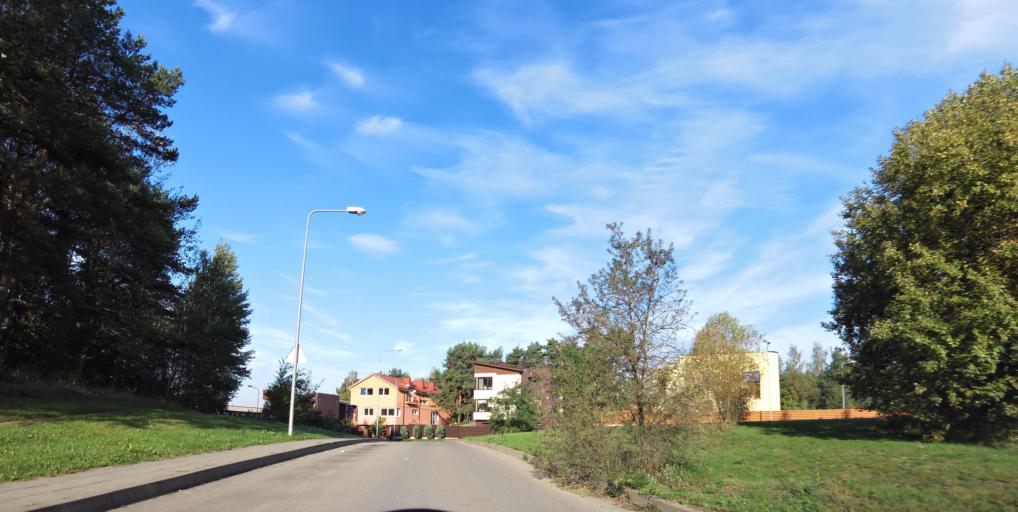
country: LT
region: Vilnius County
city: Pilaite
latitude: 54.7028
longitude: 25.1665
